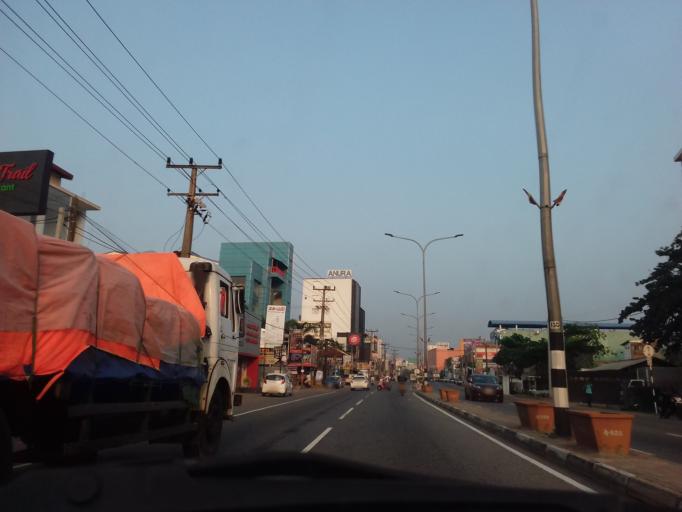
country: LK
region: Western
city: Kelaniya
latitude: 6.9732
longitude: 79.9191
